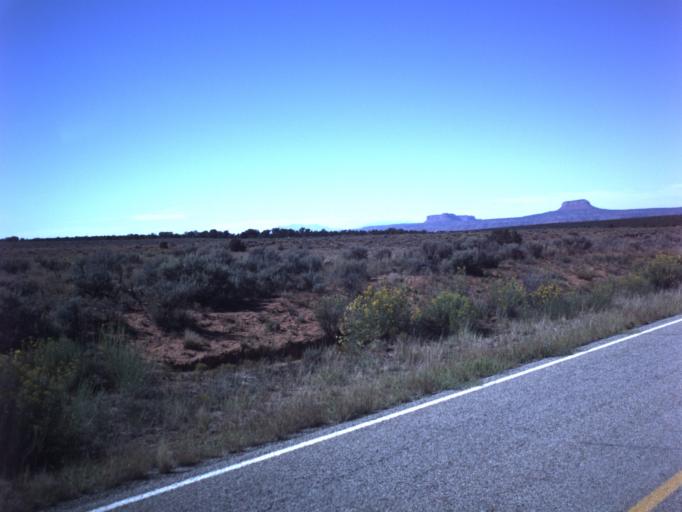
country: US
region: Utah
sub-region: San Juan County
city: Blanding
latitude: 37.3967
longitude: -109.9440
